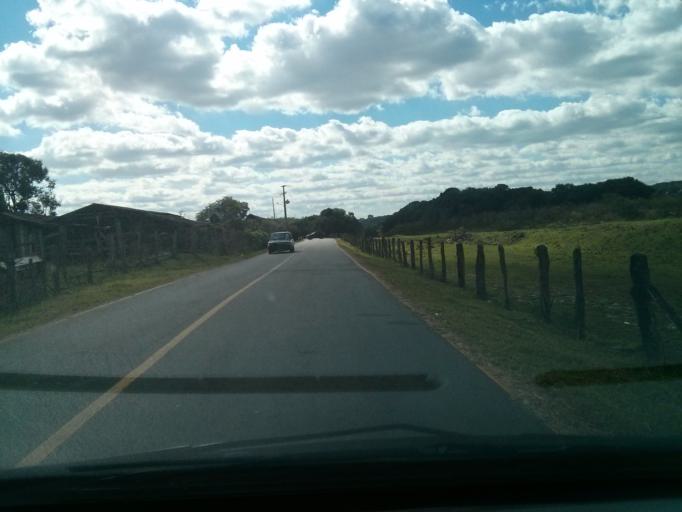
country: BR
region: Parana
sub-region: Sao Jose Dos Pinhais
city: Sao Jose dos Pinhais
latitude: -25.5532
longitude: -49.2265
